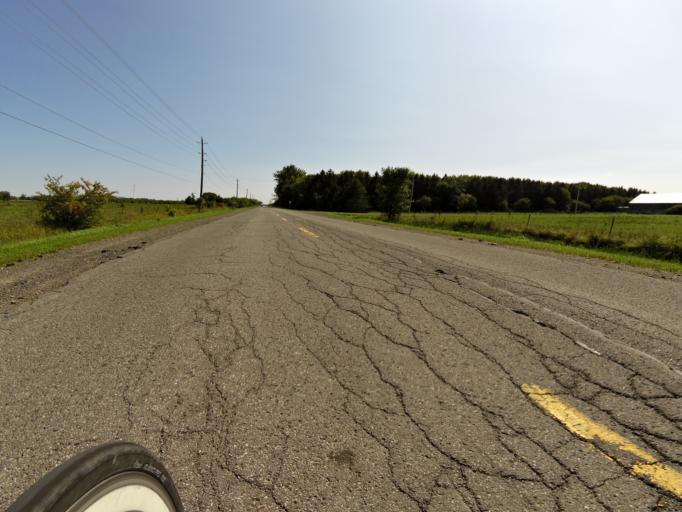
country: CA
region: Ontario
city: Arnprior
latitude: 45.4776
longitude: -76.1190
